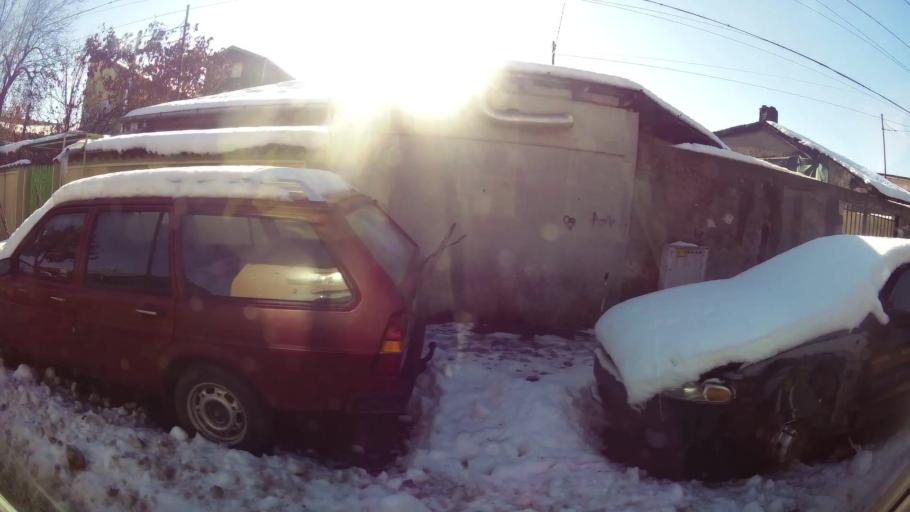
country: RO
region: Ilfov
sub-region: Comuna Magurele
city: Magurele
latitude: 44.3965
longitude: 26.0527
